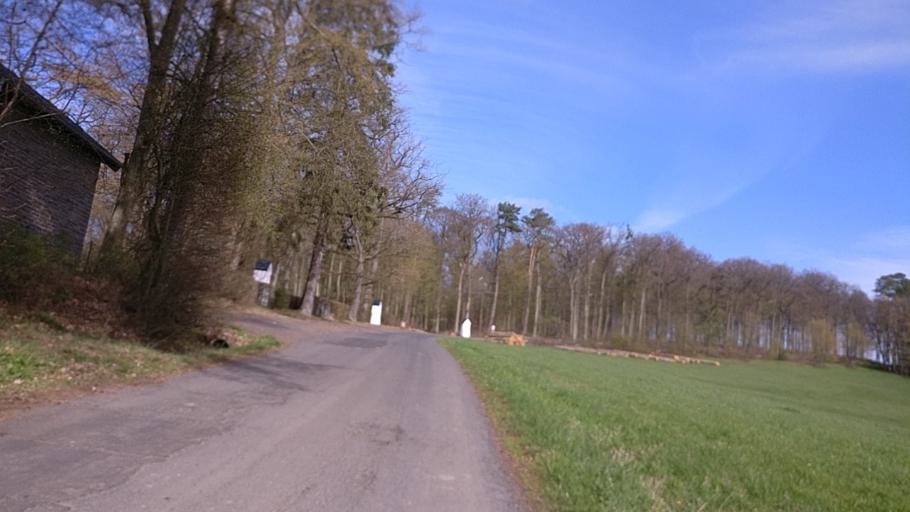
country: DE
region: Rheinland-Pfalz
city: Peterslahr
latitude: 50.6205
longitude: 7.4529
